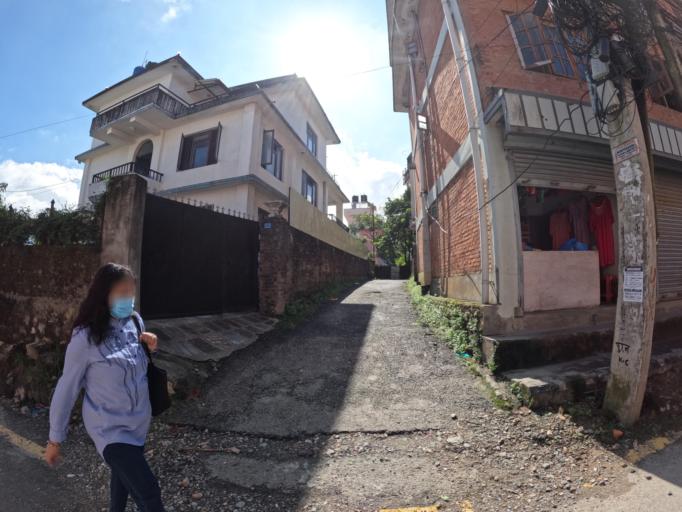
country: NP
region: Central Region
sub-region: Bagmati Zone
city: Kathmandu
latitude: 27.7508
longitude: 85.3385
